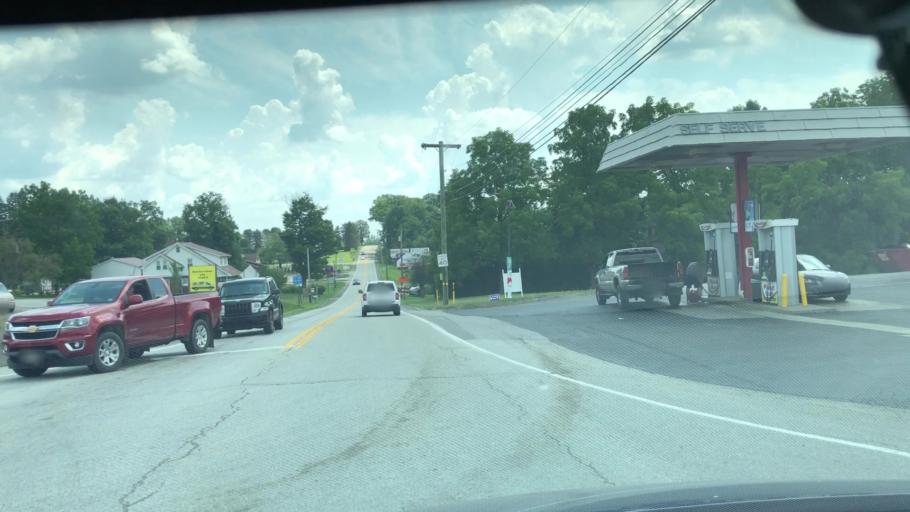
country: US
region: Pennsylvania
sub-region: Butler County
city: Saxonburg
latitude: 40.7601
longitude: -79.7788
